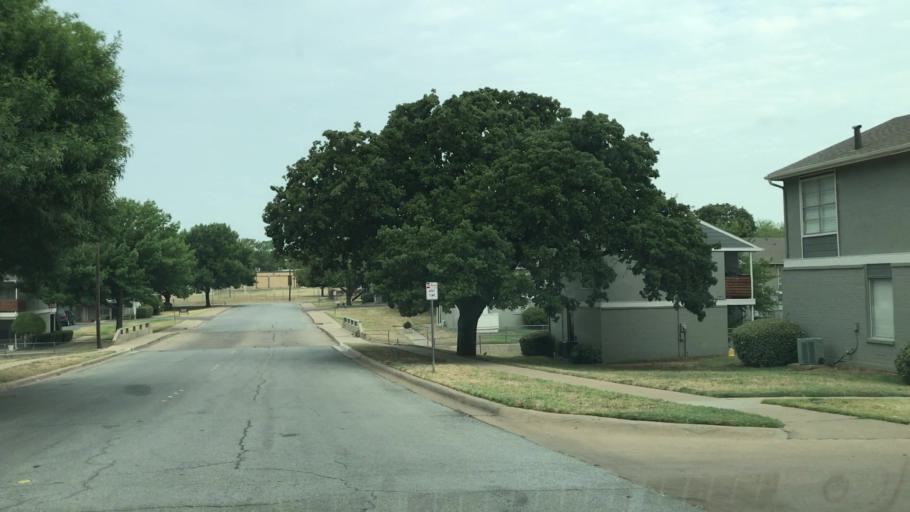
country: US
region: Texas
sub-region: Tarrant County
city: Hurst
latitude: 32.8261
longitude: -97.1663
